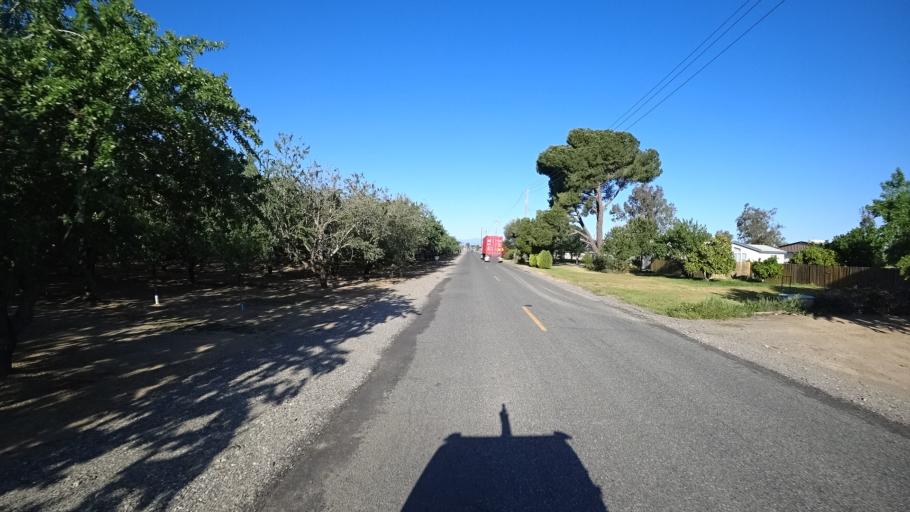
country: US
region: California
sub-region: Glenn County
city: Orland
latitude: 39.7110
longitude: -122.1756
